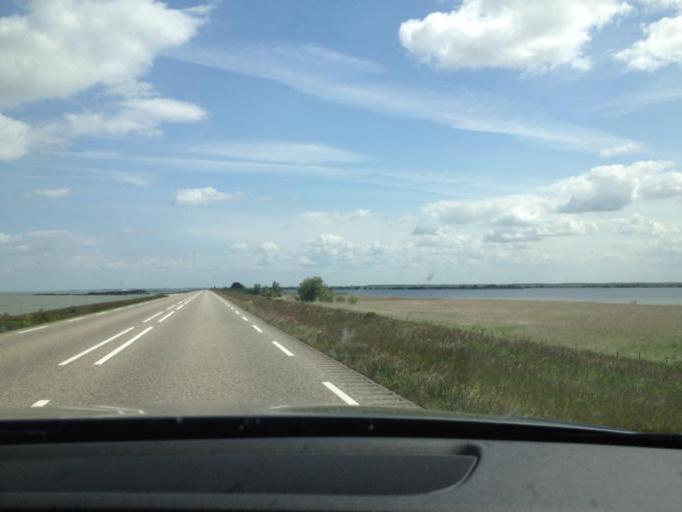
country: NL
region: Flevoland
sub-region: Gemeente Almere
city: Almere Stad
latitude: 52.4629
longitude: 5.3229
